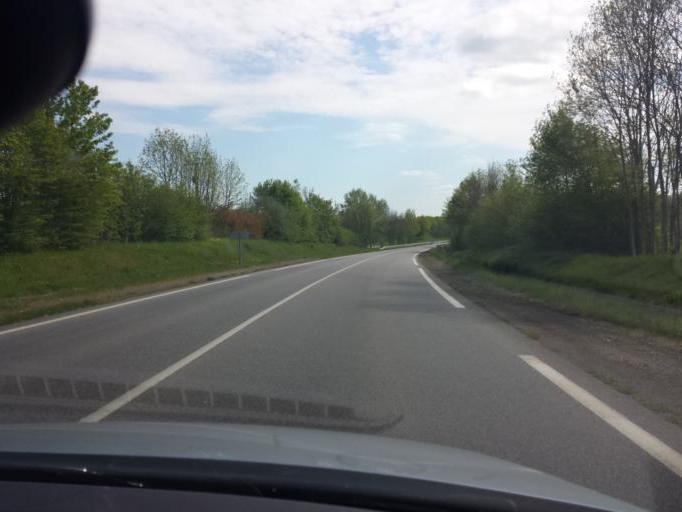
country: FR
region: Haute-Normandie
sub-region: Departement de l'Eure
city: Breteuil
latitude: 48.8381
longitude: 0.9372
